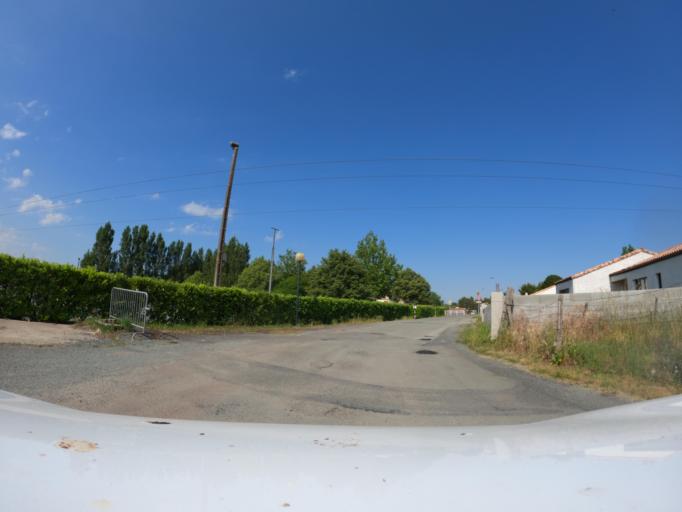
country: FR
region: Pays de la Loire
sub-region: Departement de la Vendee
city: Champagne-les-Marais
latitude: 46.3804
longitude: -1.1106
